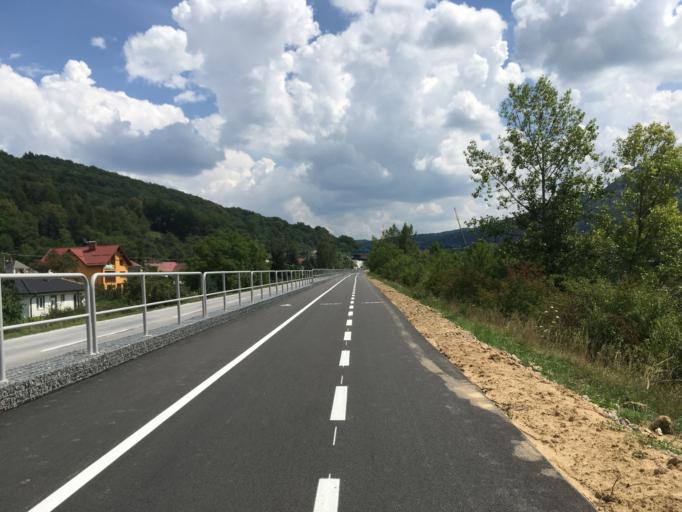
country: SK
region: Nitriansky
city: Puchov
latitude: 49.1372
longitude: 18.3571
